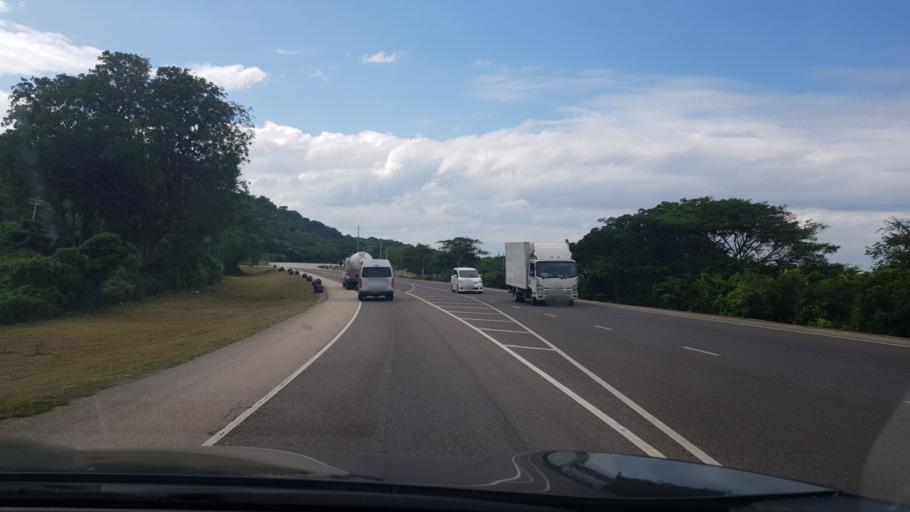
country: JM
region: Trelawny
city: Falmouth
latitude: 18.4838
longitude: -77.6005
